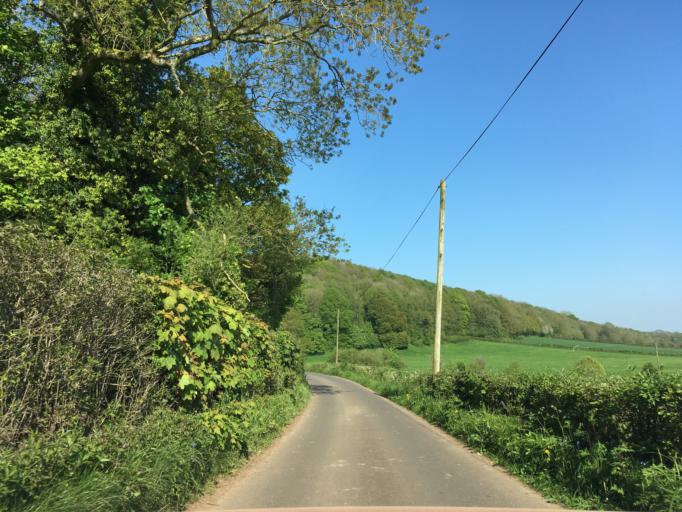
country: GB
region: Wales
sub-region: Newport
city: Llanvaches
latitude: 51.6284
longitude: -2.7873
